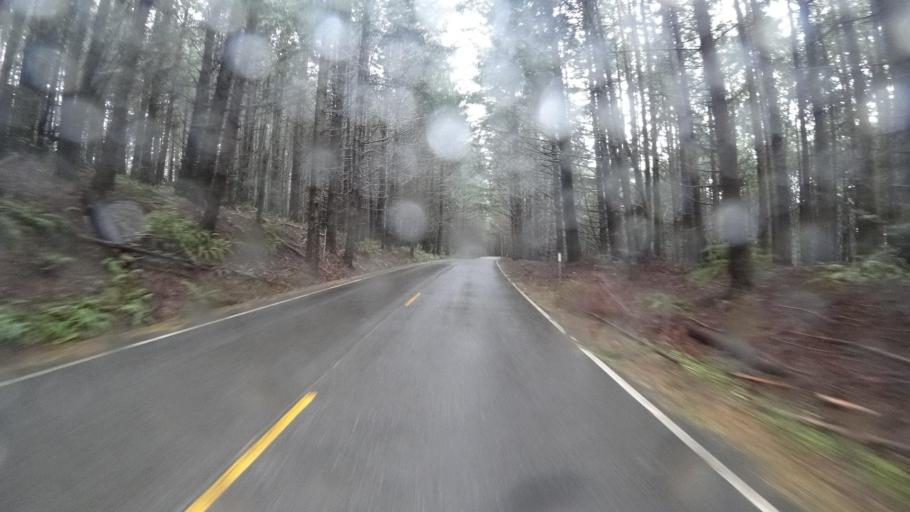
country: US
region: California
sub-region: Humboldt County
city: Westhaven-Moonstone
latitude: 41.2172
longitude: -123.9571
